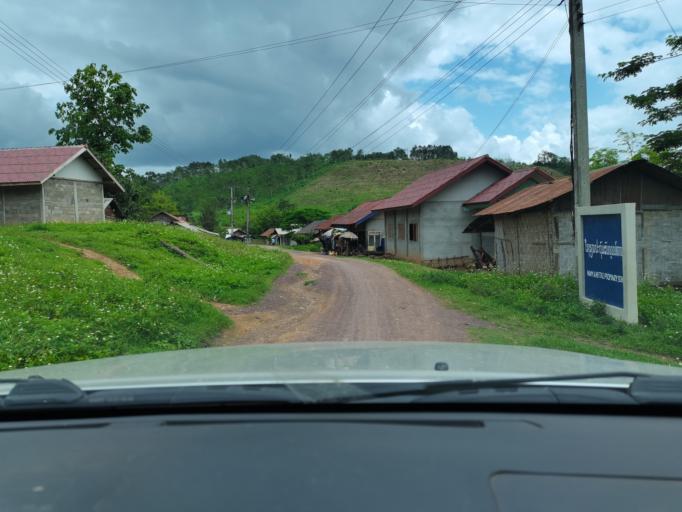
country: LA
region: Loungnamtha
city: Muang Long
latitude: 20.7059
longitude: 101.0099
